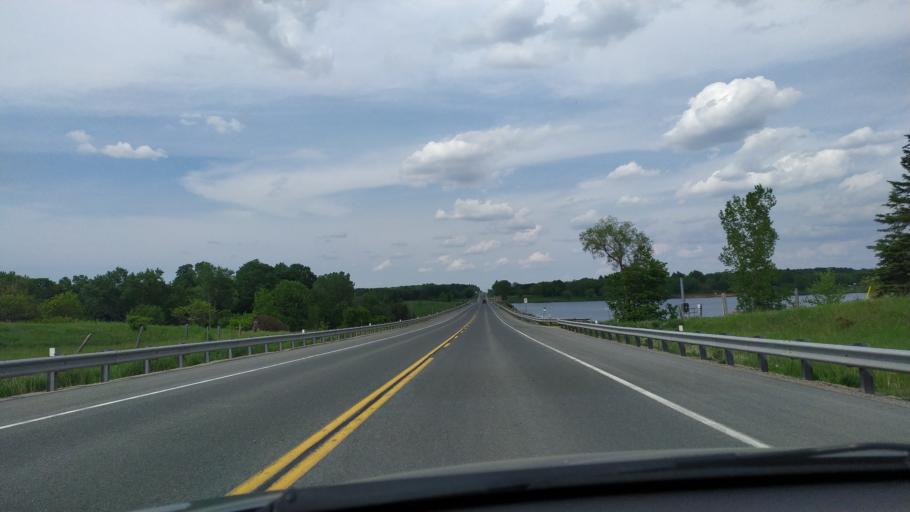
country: CA
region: Ontario
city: Stratford
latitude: 43.2594
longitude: -81.0769
